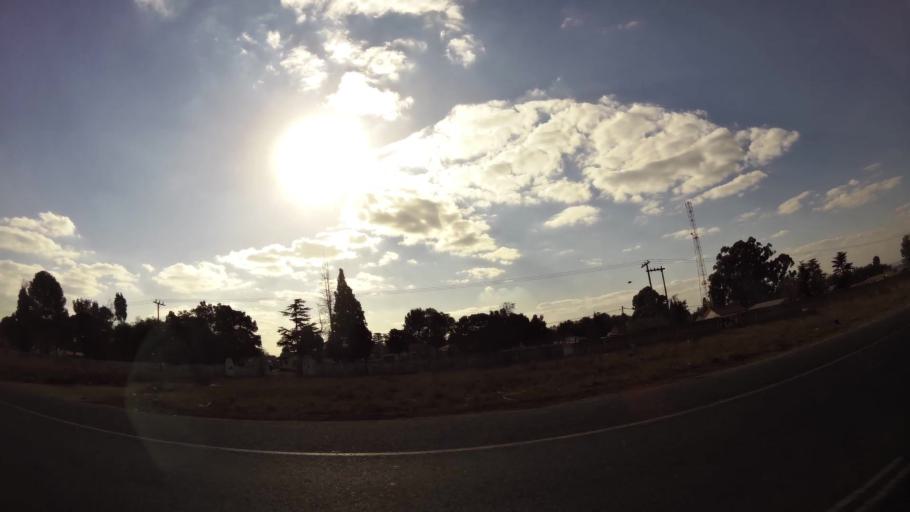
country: ZA
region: Gauteng
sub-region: City of Johannesburg Metropolitan Municipality
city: Midrand
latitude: -26.0116
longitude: 28.1654
